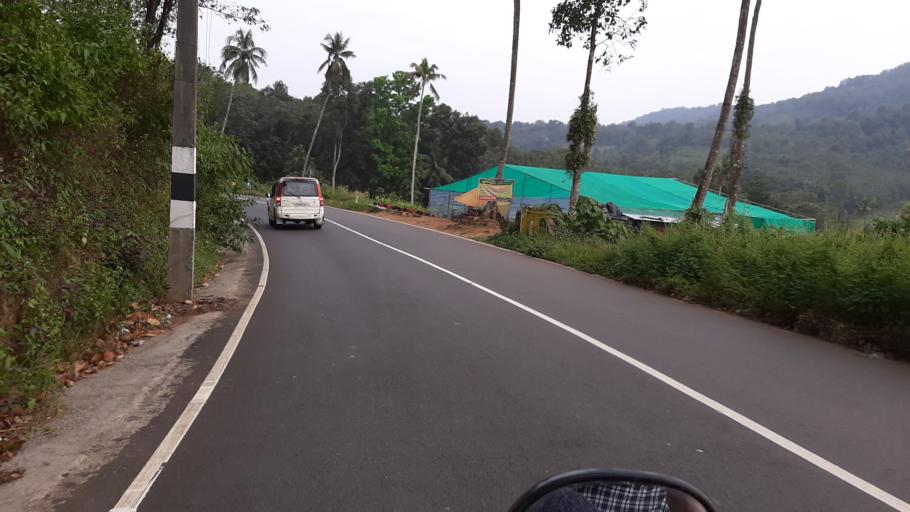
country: IN
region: Kerala
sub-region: Pattanamtitta
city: Pathanamthitta
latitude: 9.4521
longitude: 76.8691
